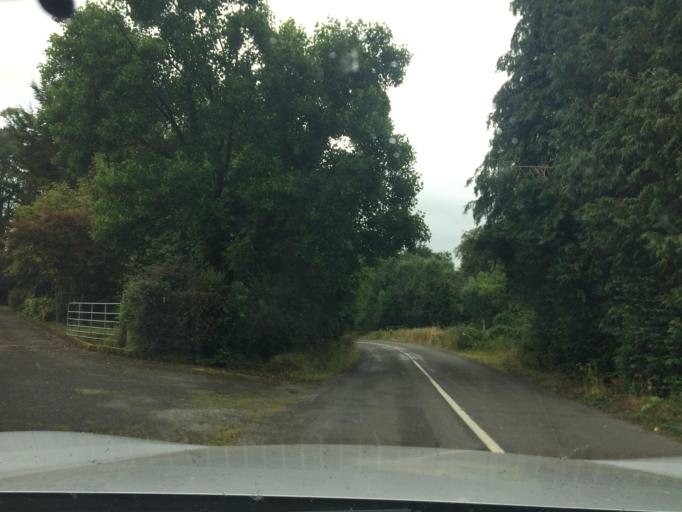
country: IE
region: Munster
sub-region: South Tipperary
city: Cluain Meala
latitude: 52.2243
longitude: -7.7256
